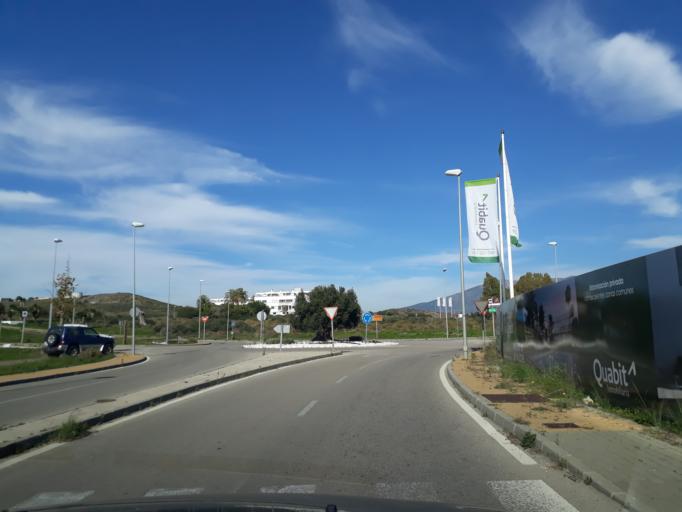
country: ES
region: Andalusia
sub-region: Provincia de Malaga
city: Fuengirola
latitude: 36.5246
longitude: -4.6867
